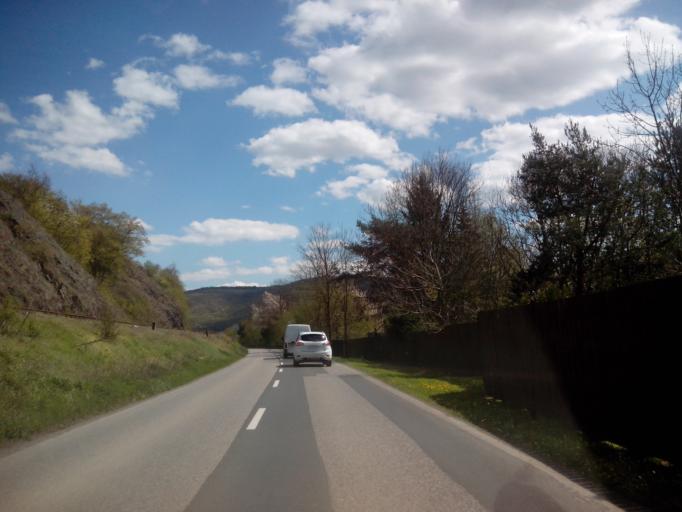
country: CZ
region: Central Bohemia
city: Hyskov
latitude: 49.9940
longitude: 14.0275
